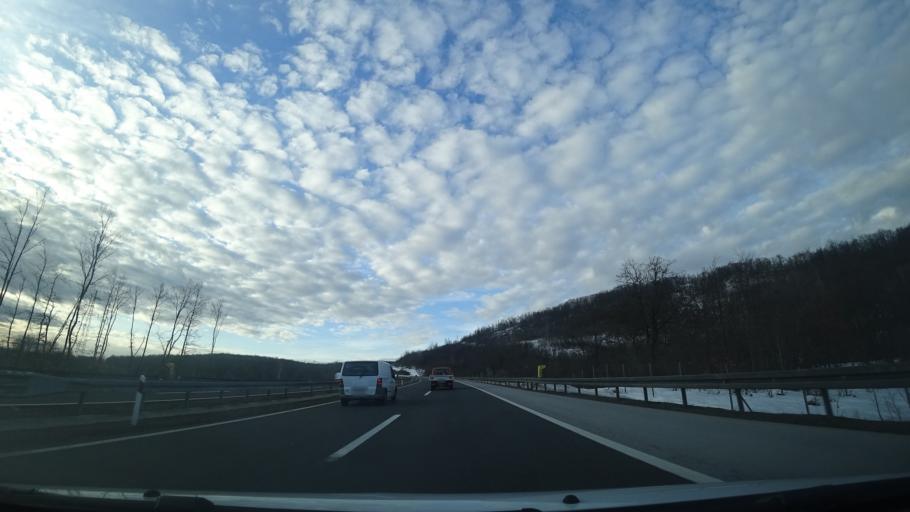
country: HR
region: Karlovacka
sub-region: Grad Ogulin
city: Ogulin
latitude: 45.2898
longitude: 15.2740
